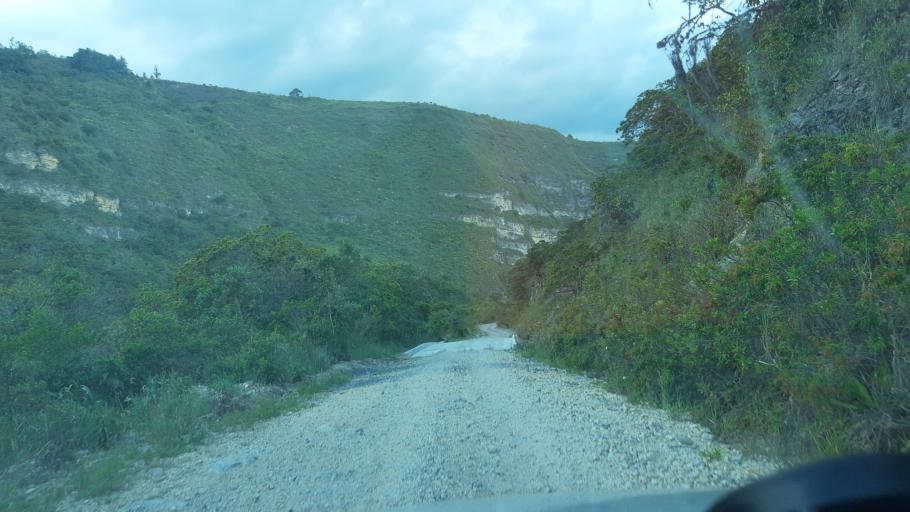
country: CO
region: Boyaca
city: Santa Sofia
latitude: 5.7447
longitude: -73.5771
